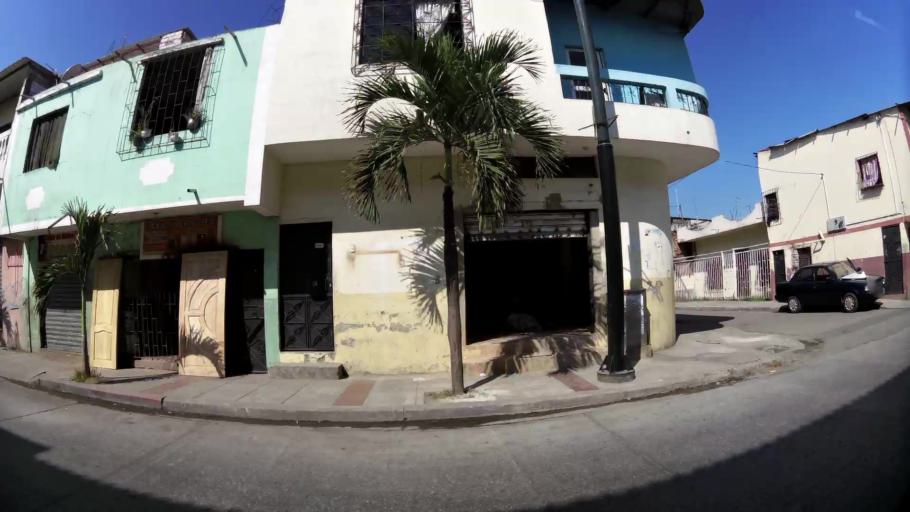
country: EC
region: Guayas
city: Santa Lucia
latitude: -2.0990
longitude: -79.9331
